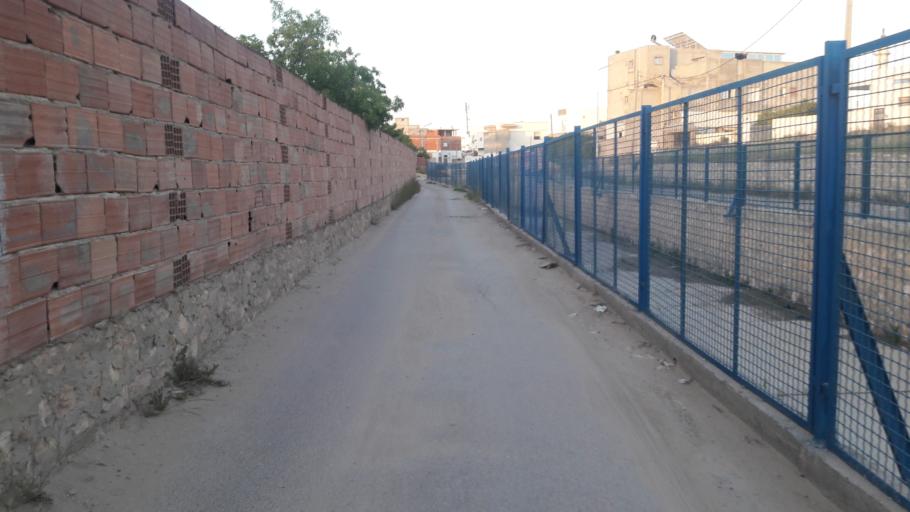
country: TN
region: Safaqis
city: Al Qarmadah
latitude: 34.8083
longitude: 10.7473
